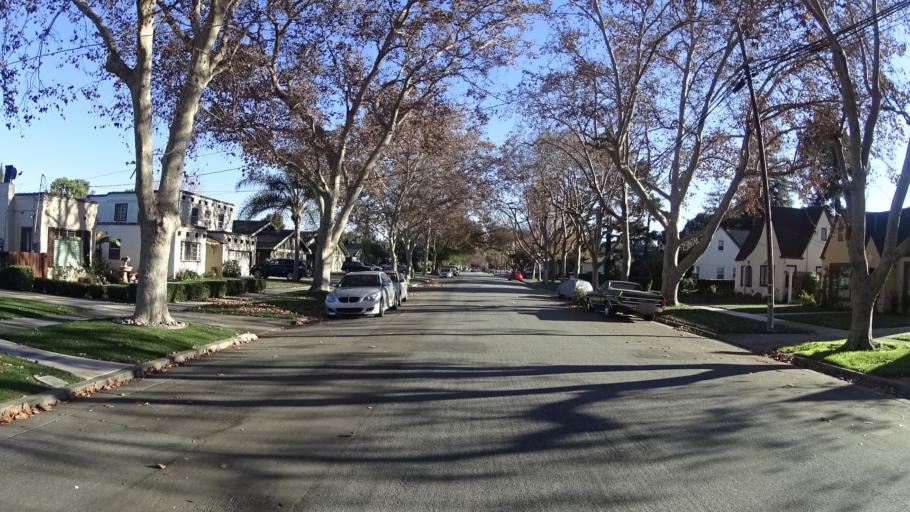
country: US
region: California
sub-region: Santa Clara County
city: San Jose
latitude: 37.3576
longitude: -121.9037
